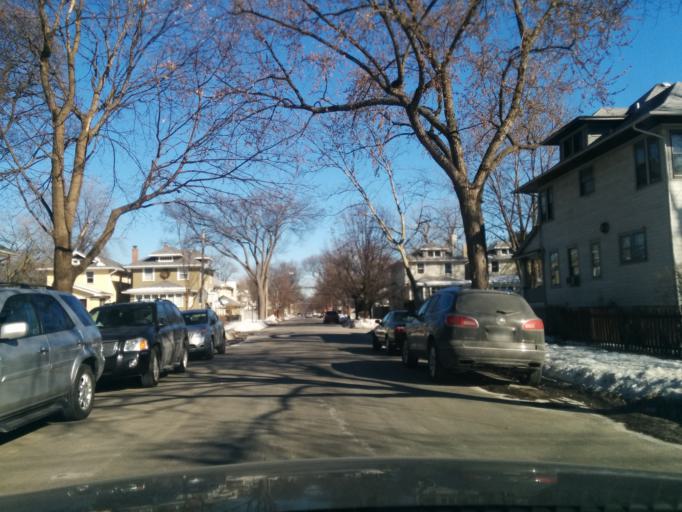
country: US
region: Illinois
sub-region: Cook County
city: Oak Park
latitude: 41.8744
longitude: -87.7885
